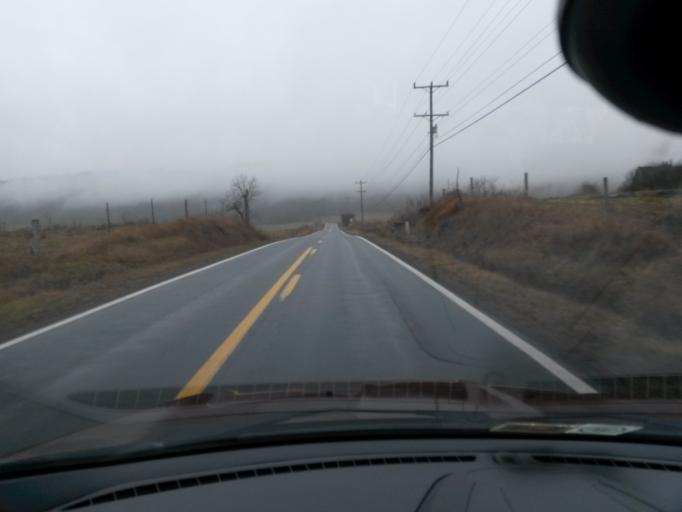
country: US
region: West Virginia
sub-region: Greenbrier County
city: Lewisburg
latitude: 37.8742
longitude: -80.5226
